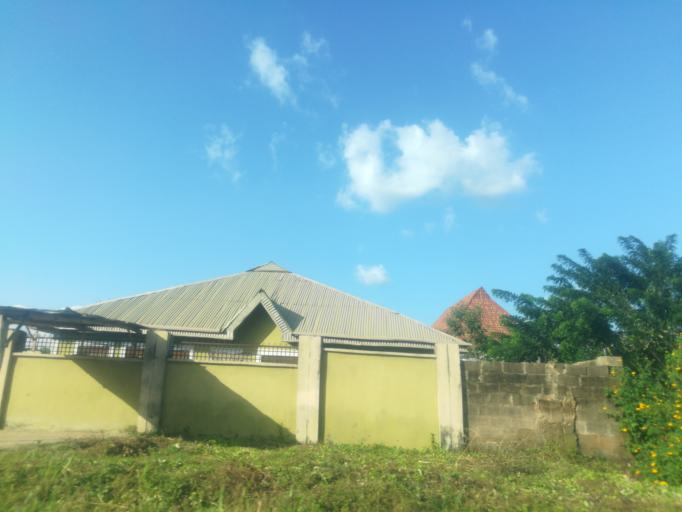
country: NG
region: Oyo
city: Ibadan
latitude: 7.4368
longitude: 3.9697
